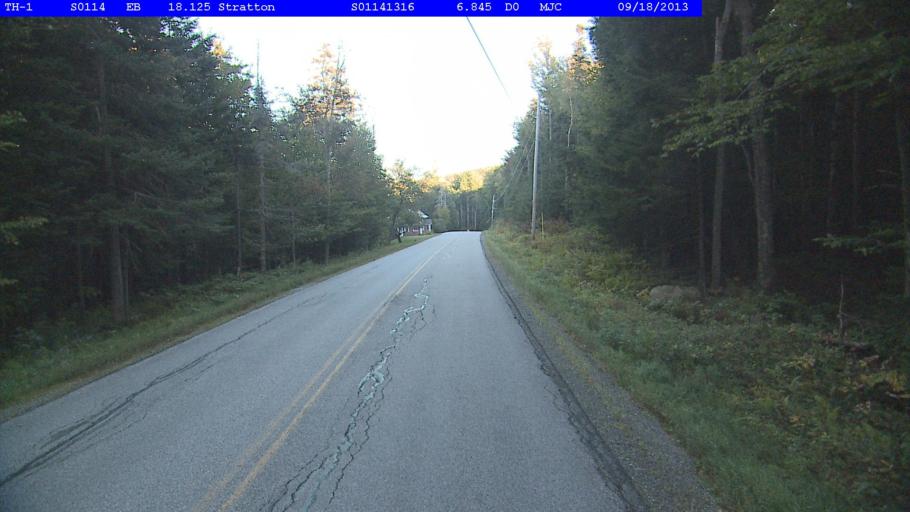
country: US
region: Vermont
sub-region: Windham County
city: Dover
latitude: 43.0289
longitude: -72.8852
